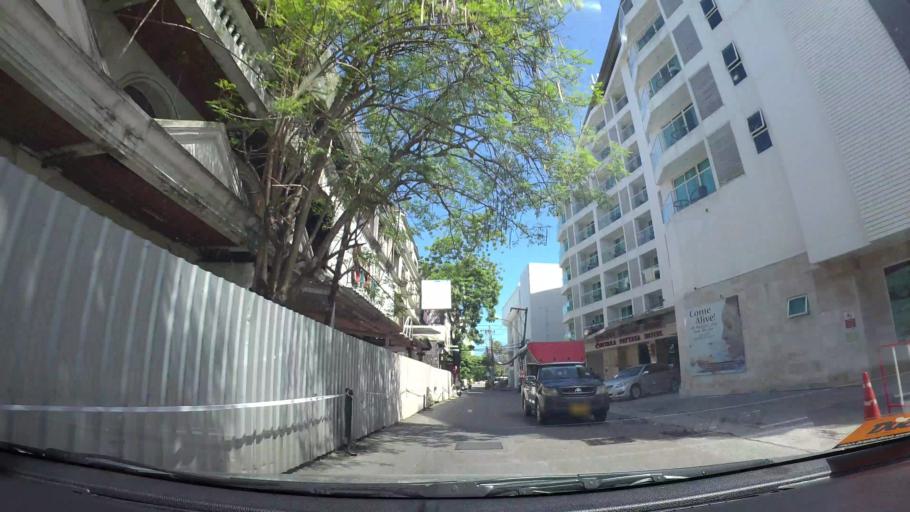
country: TH
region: Chon Buri
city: Phatthaya
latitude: 12.9411
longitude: 100.8885
